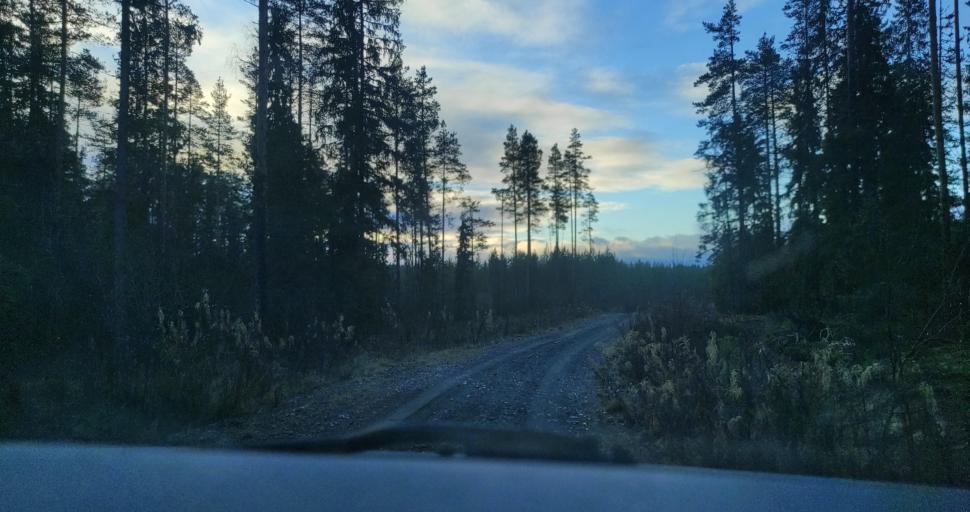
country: RU
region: Republic of Karelia
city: Pitkyaranta
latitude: 61.7399
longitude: 31.3644
